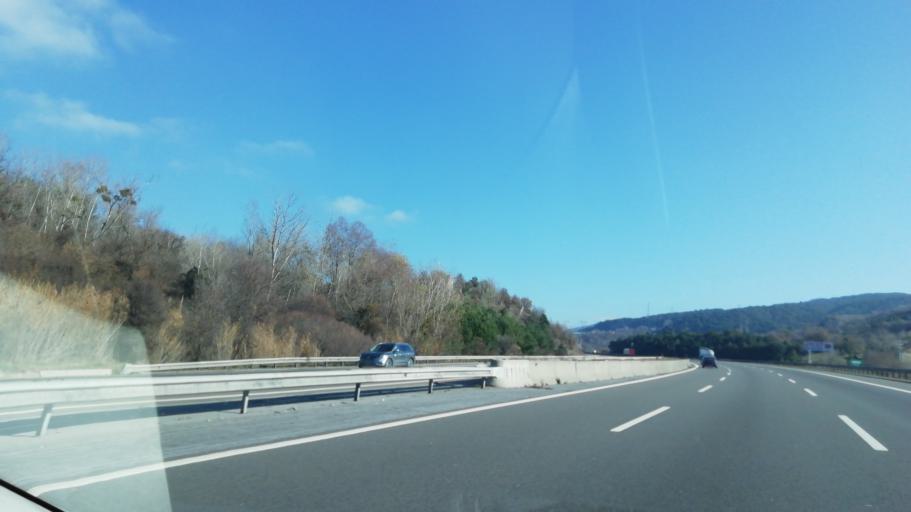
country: TR
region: Bolu
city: Bolu
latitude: 40.7341
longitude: 31.8058
